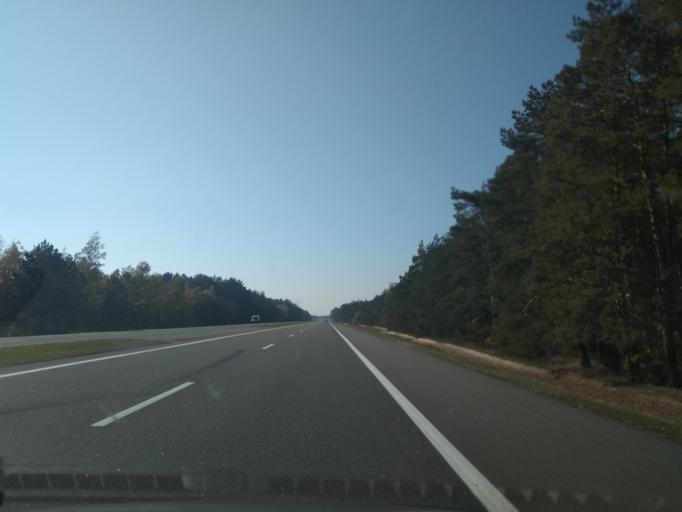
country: BY
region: Brest
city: Antopal'
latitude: 52.3613
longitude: 24.7179
